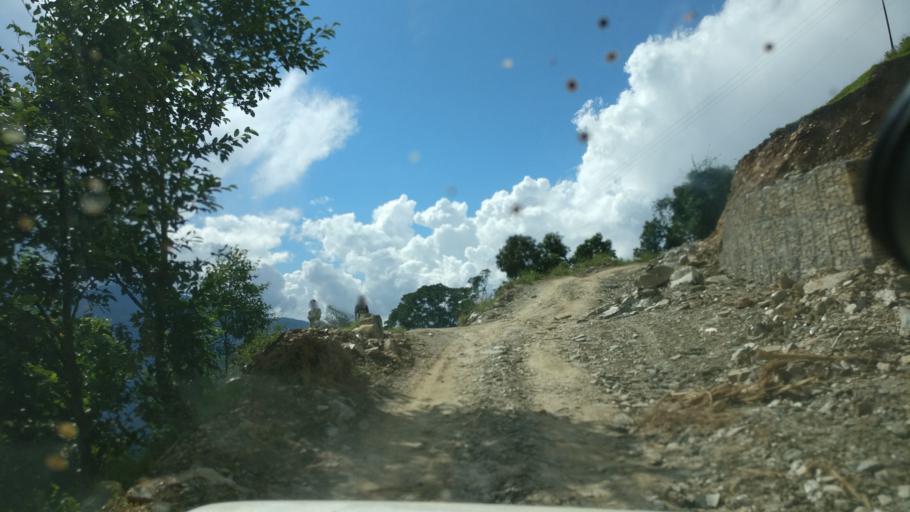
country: NP
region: Western Region
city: Baglung
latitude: 28.2635
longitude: 83.6411
